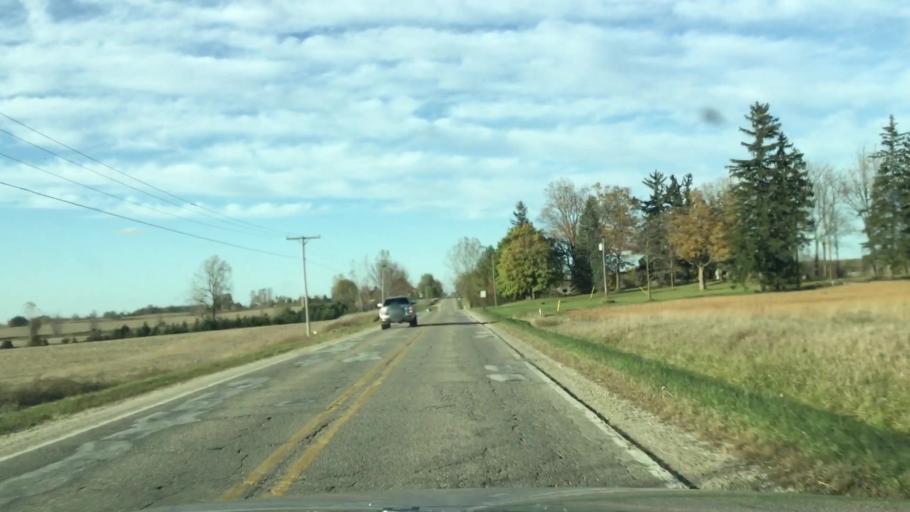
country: US
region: Michigan
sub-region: Lapeer County
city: North Branch
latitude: 43.2414
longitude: -83.1974
